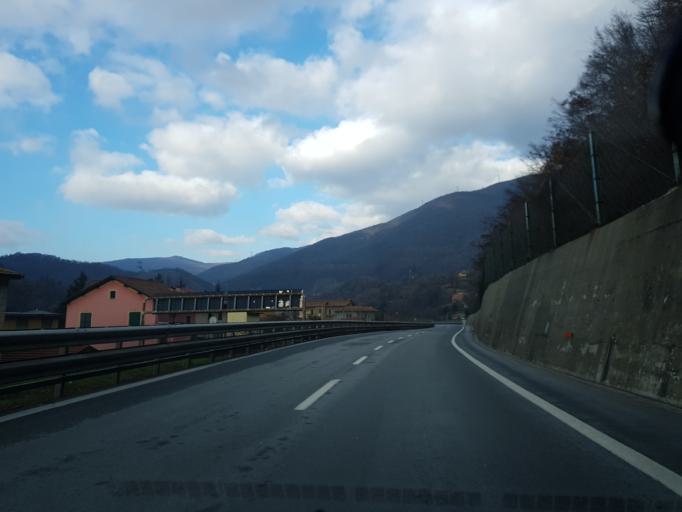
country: IT
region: Liguria
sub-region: Provincia di Genova
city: Isola del Cantone
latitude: 44.6422
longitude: 8.9579
